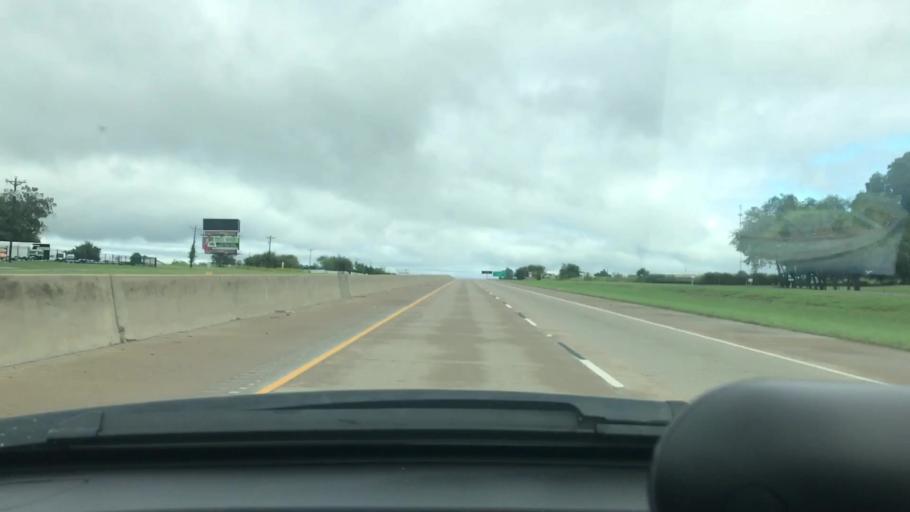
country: US
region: Texas
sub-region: Grayson County
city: Van Alstyne
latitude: 33.4453
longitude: -96.6017
